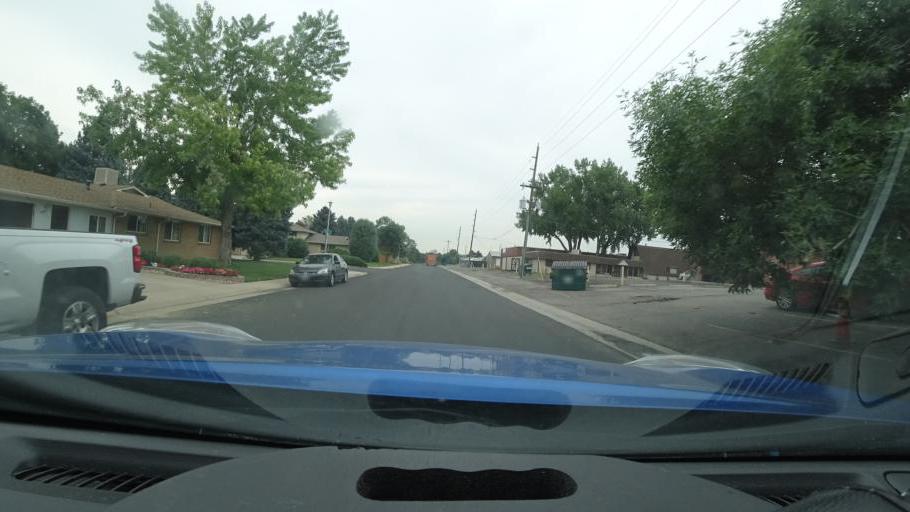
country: US
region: Colorado
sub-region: Arapahoe County
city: Glendale
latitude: 39.6803
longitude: -104.9077
